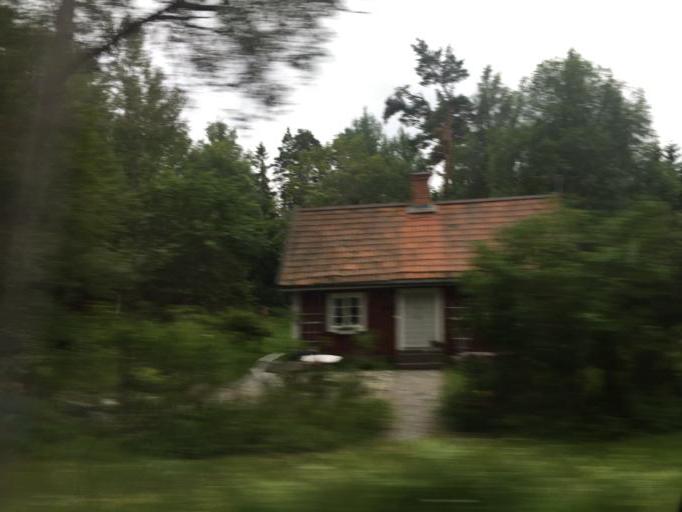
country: SE
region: OErebro
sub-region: Orebro Kommun
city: Odensbacken
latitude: 59.0210
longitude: 15.6310
